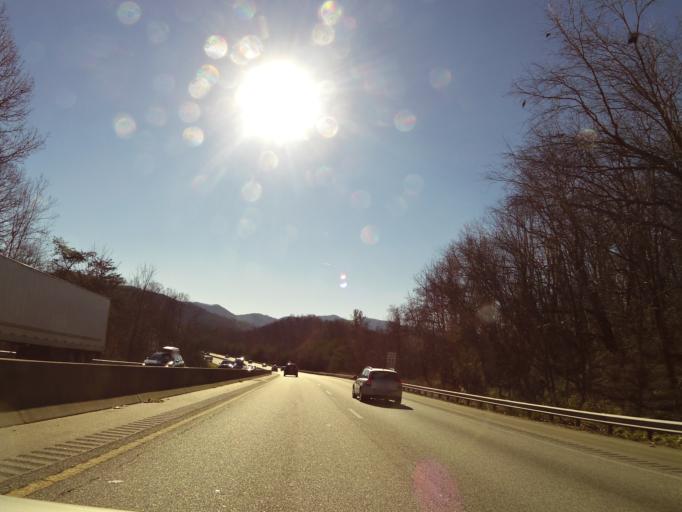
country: US
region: North Carolina
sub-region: Haywood County
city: Canton
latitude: 35.5455
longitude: -82.8146
